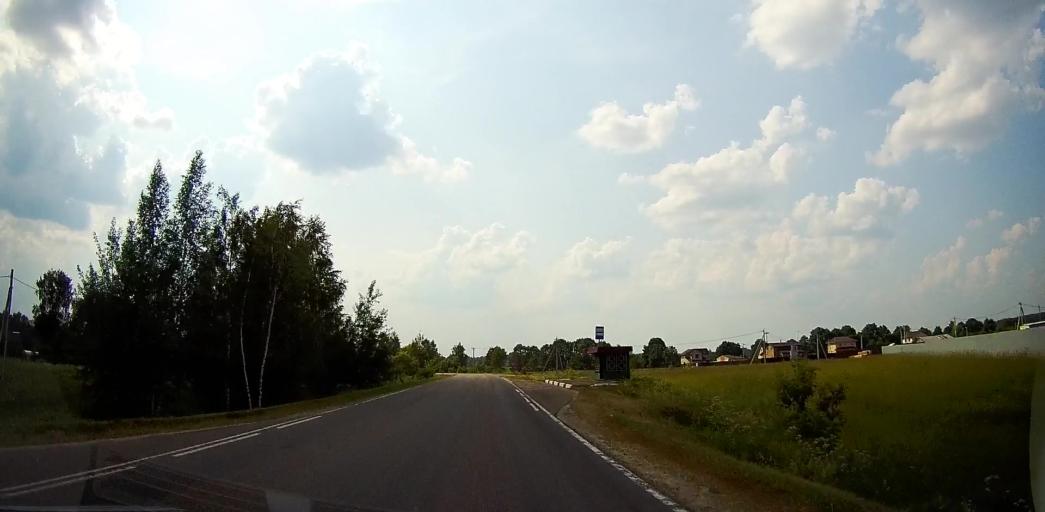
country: RU
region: Moskovskaya
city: Malino
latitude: 55.0643
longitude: 38.1085
